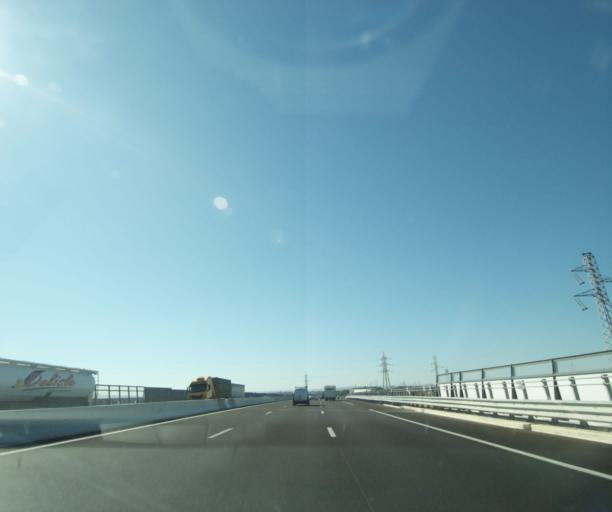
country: FR
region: Languedoc-Roussillon
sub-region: Departement de l'Herault
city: Lattes
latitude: 43.5709
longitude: 3.8675
